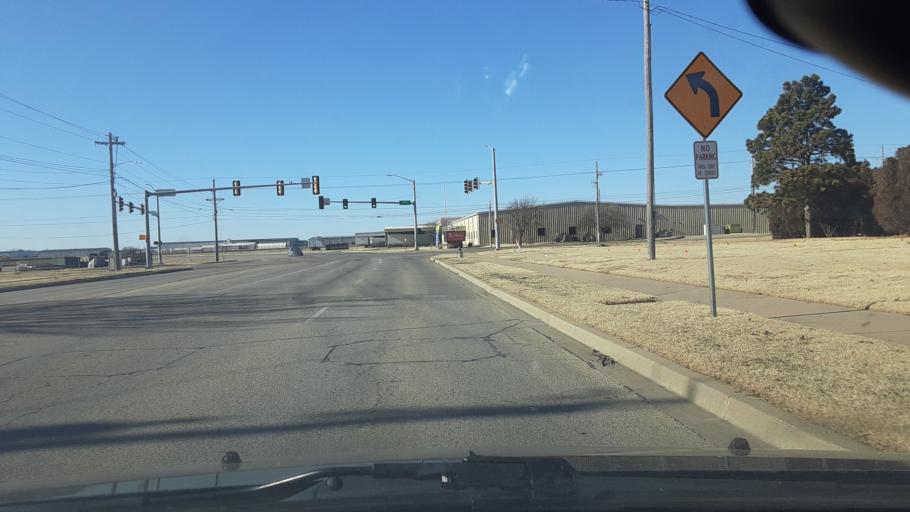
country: US
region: Oklahoma
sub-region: Kay County
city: Ponca City
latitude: 36.7243
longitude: -97.0941
